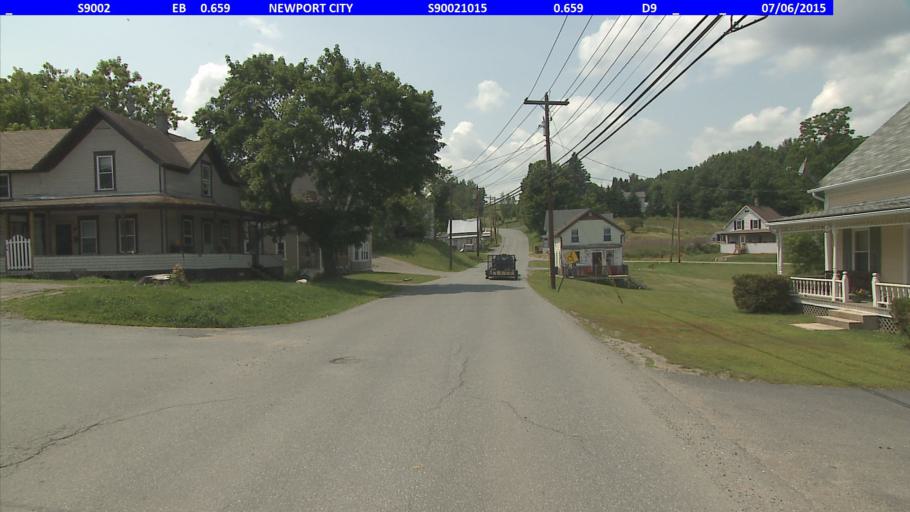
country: US
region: Vermont
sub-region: Orleans County
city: Newport
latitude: 44.9369
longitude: -72.2198
